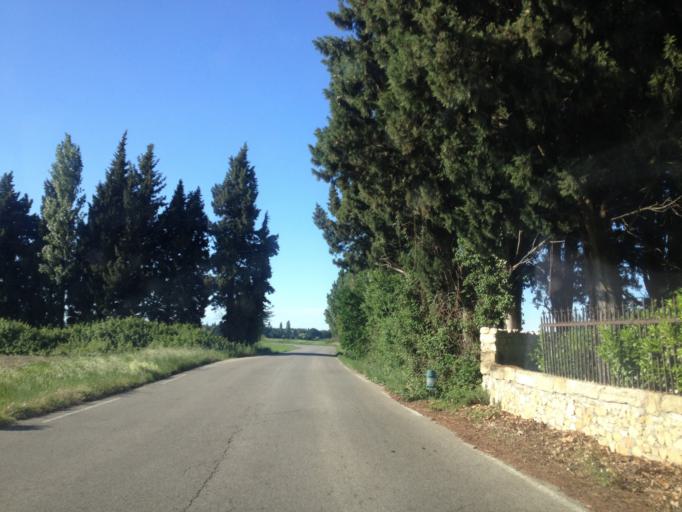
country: FR
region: Provence-Alpes-Cote d'Azur
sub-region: Departement du Vaucluse
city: Orange
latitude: 44.1359
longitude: 4.8414
